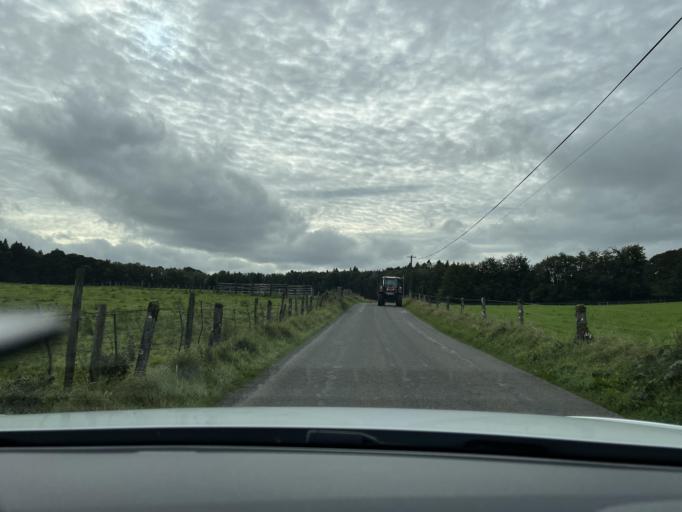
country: IE
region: Connaught
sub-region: Roscommon
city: Boyle
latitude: 53.9778
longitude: -8.2549
